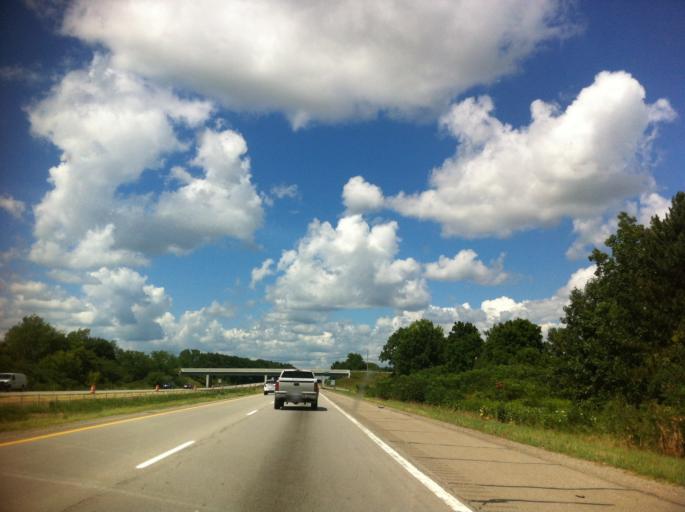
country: US
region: Michigan
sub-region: Washtenaw County
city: Milan
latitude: 42.1687
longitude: -83.6843
